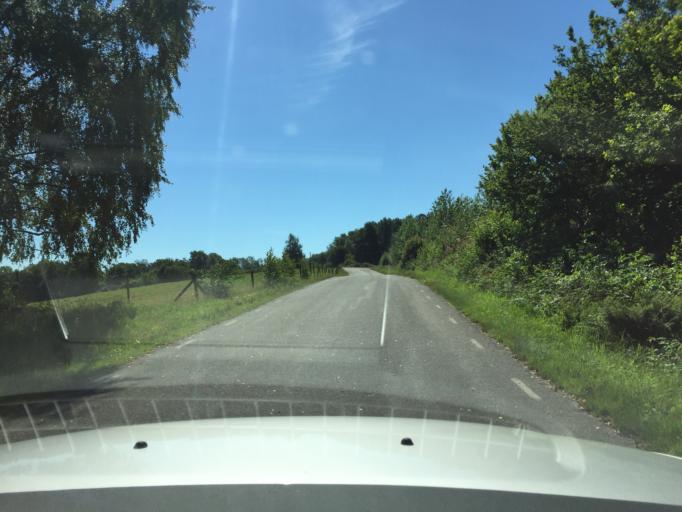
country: SE
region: Skane
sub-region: Hassleholms Kommun
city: Sosdala
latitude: 56.0187
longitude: 13.5863
